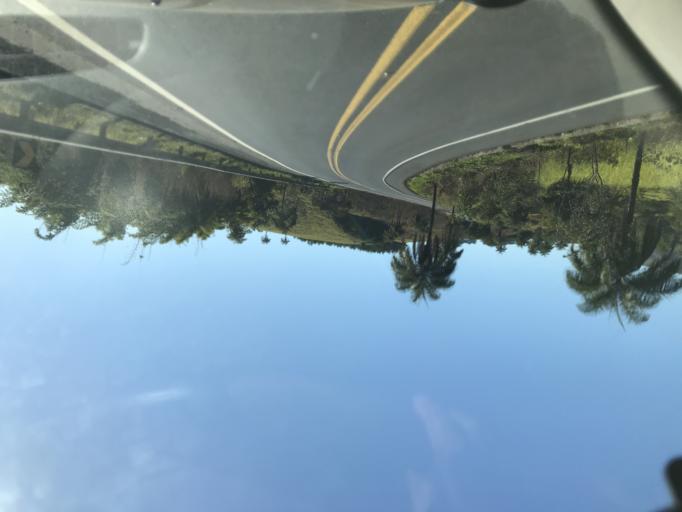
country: BR
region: Minas Gerais
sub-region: Campos Altos
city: Campos Altos
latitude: -19.8177
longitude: -46.0215
